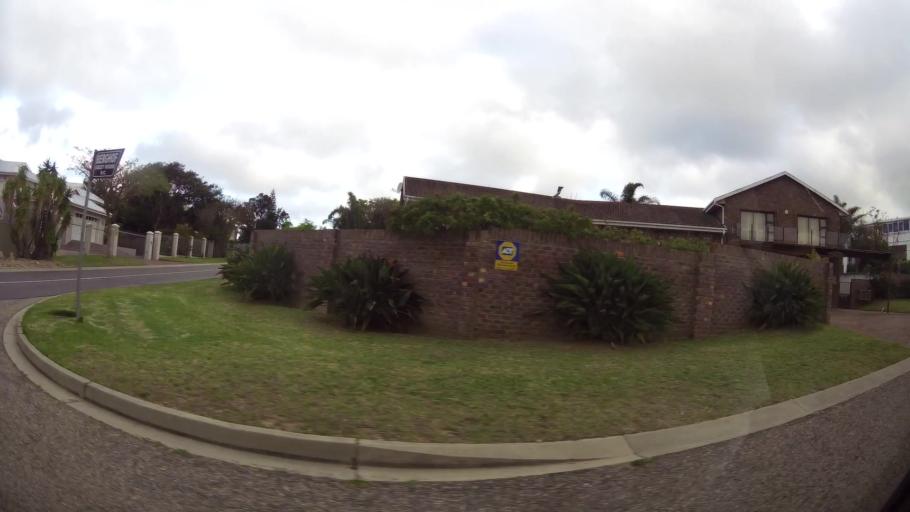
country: ZA
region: Western Cape
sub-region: Eden District Municipality
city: Plettenberg Bay
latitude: -34.0551
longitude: 23.3622
